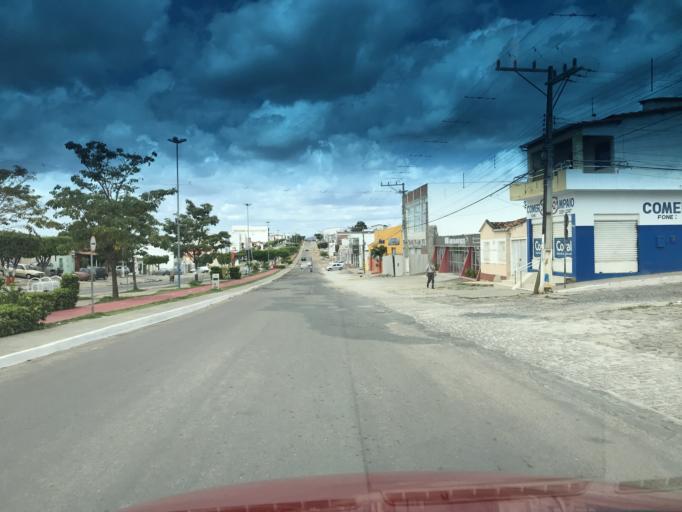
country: BR
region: Bahia
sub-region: Itaberaba
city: Itaberaba
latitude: -12.5215
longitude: -40.3061
